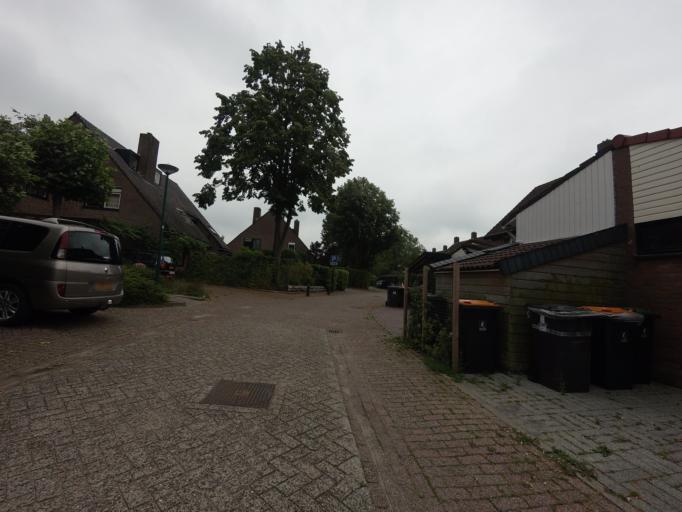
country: NL
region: Utrecht
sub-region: Gemeente Wijk bij Duurstede
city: Wijk bij Duurstede
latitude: 51.9837
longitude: 5.3464
